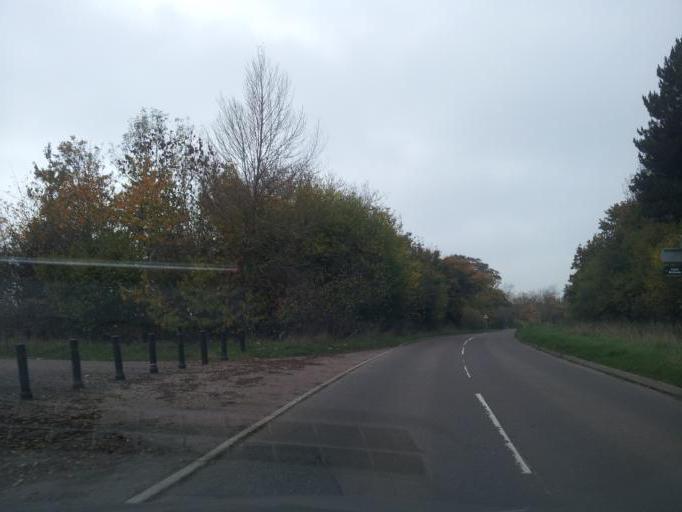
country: GB
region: England
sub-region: Milton Keynes
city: Shenley Church End
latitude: 51.9876
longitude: -0.8285
